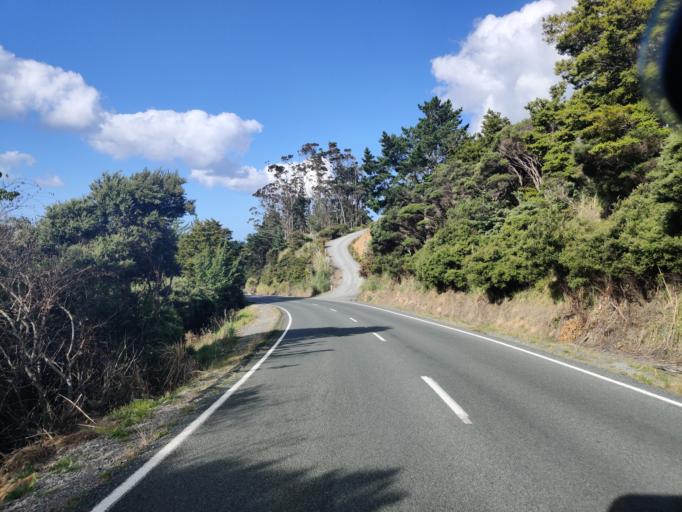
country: NZ
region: Northland
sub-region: Whangarei
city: Ngunguru
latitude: -35.6141
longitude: 174.5219
